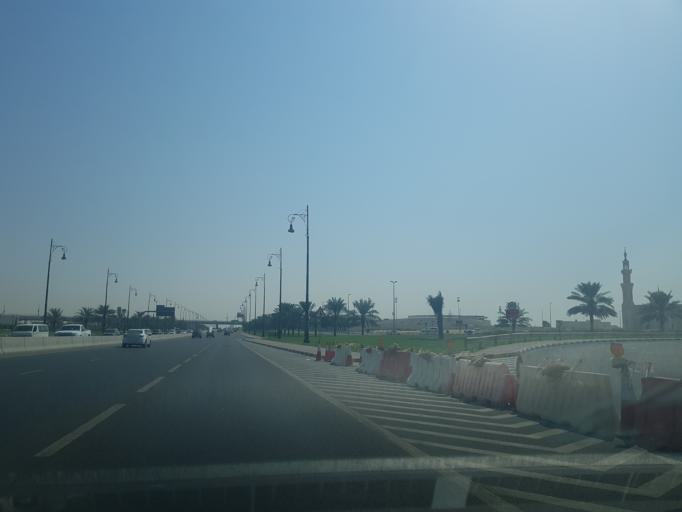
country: AE
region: Ash Shariqah
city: Sharjah
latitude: 25.3180
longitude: 55.5184
